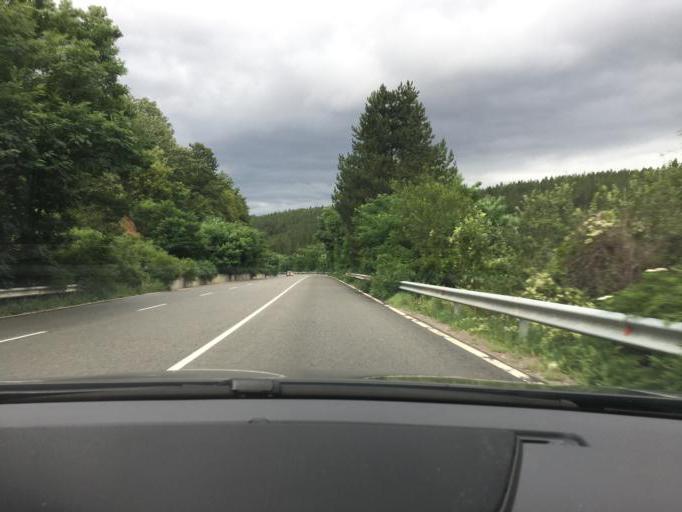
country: BG
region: Kyustendil
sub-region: Obshtina Bobovdol
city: Bobovdol
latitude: 42.2759
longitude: 22.9374
